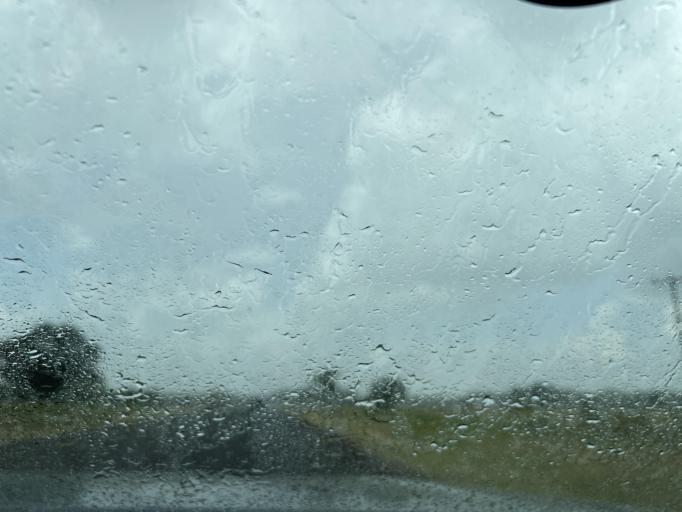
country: US
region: Texas
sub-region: Wise County
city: Boyd
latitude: 33.1387
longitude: -97.6423
